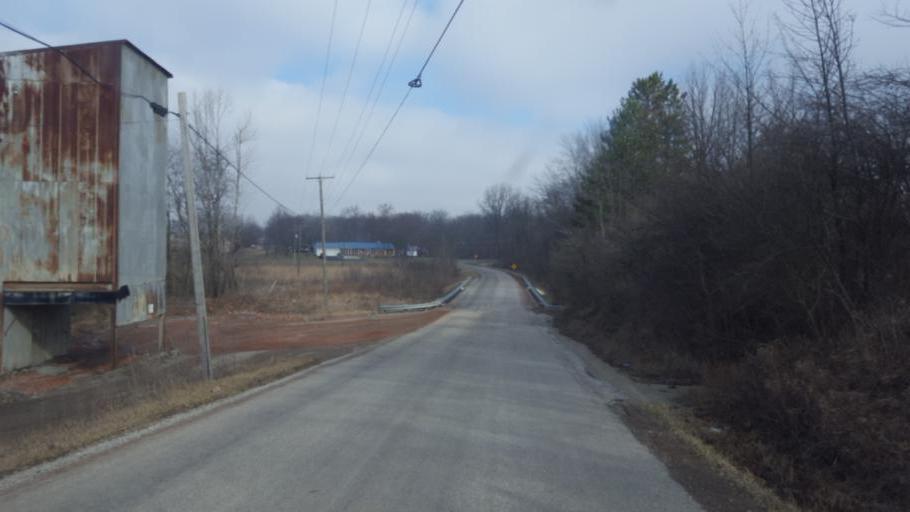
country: US
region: Ohio
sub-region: Crawford County
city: Galion
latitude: 40.6636
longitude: -82.8590
